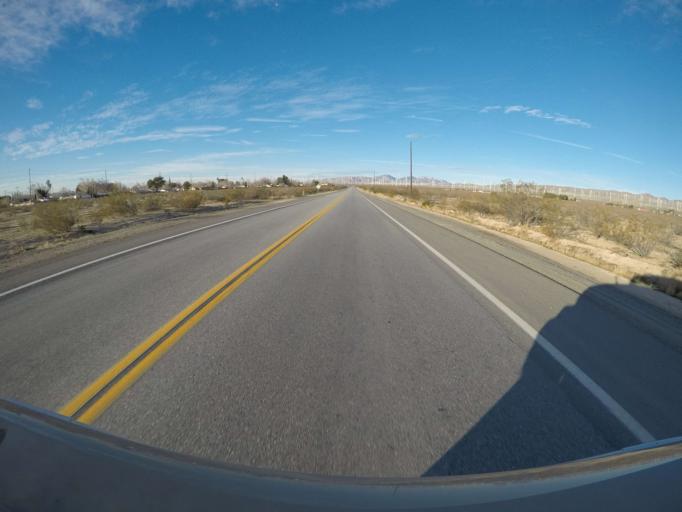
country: US
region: California
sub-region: Kern County
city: Mojave
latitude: 35.0554
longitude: -118.1872
